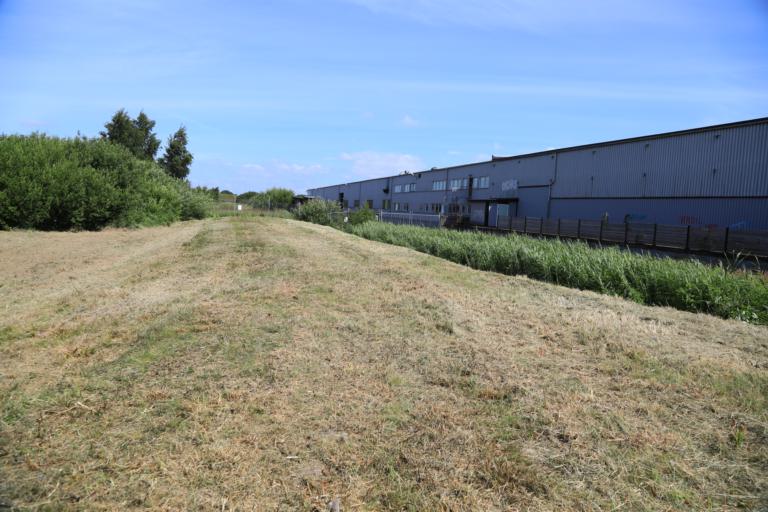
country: SE
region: Halland
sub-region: Varbergs Kommun
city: Varberg
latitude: 57.1208
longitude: 12.2554
